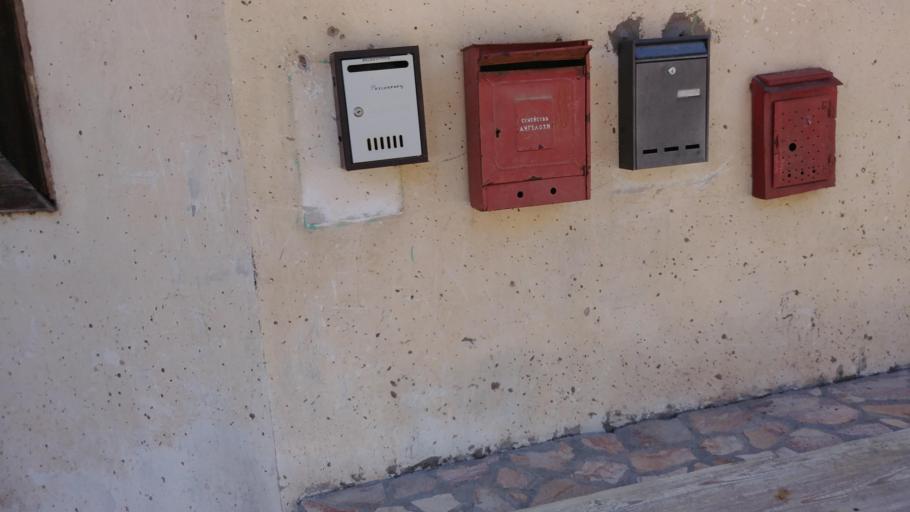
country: BG
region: Veliko Turnovo
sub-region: Obshtina Veliko Turnovo
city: Veliko Turnovo
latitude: 43.0865
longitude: 25.6401
